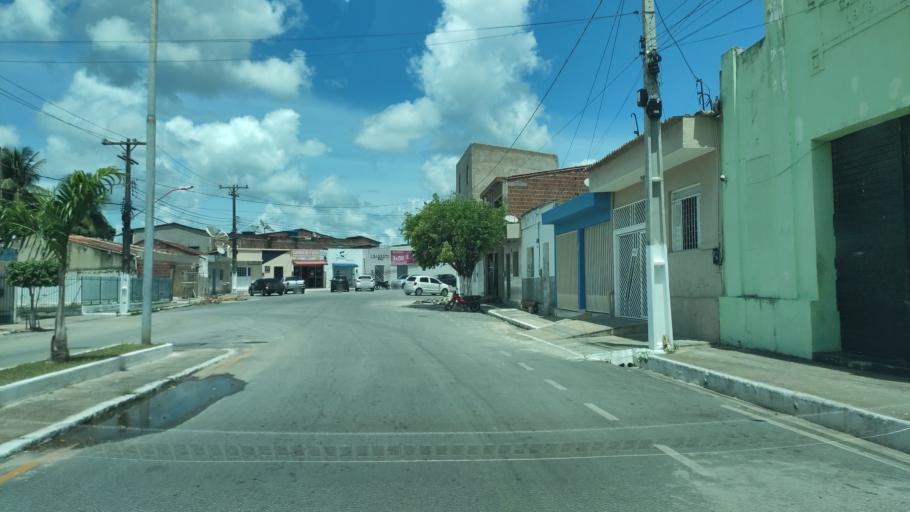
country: BR
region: Alagoas
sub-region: Uniao Dos Palmares
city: Uniao dos Palmares
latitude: -9.1623
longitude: -36.0319
